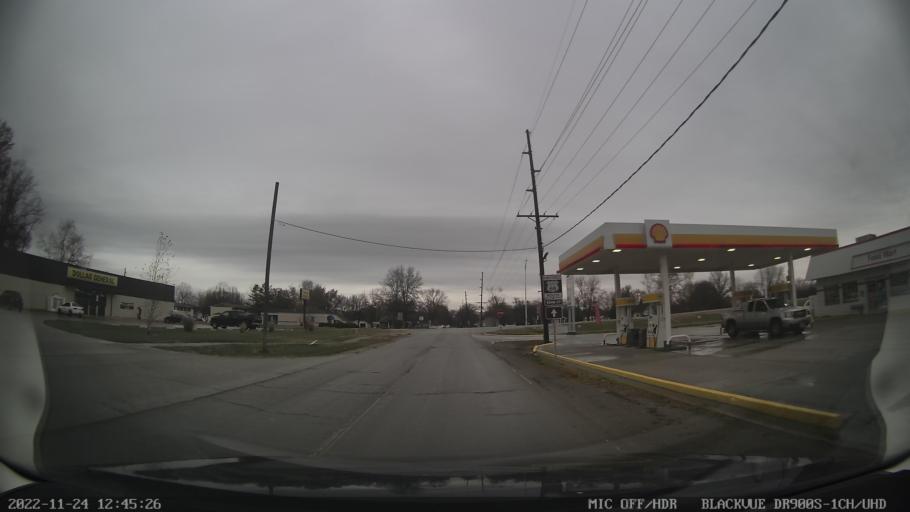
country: US
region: Illinois
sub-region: Macoupin County
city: Staunton
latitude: 38.9670
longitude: -89.7581
